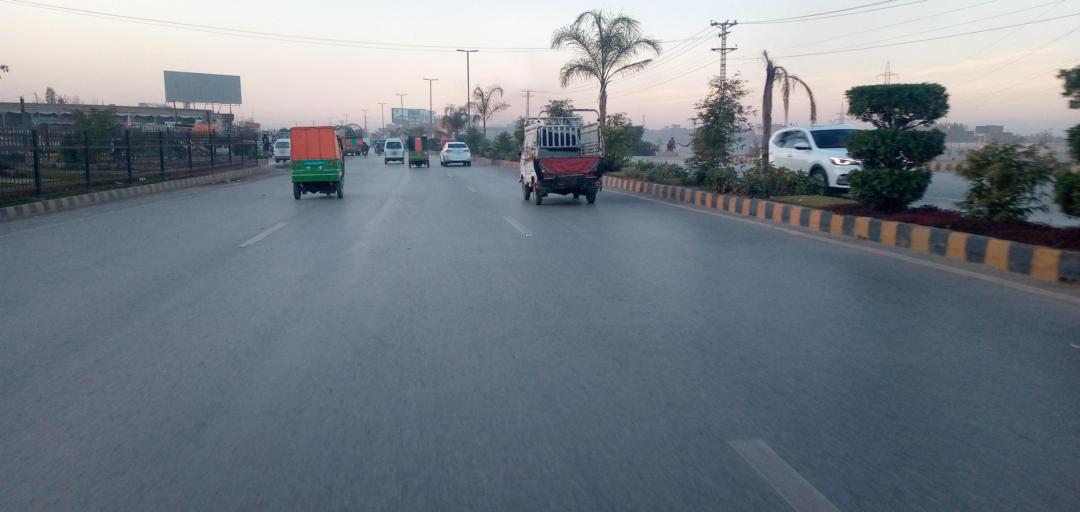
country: PK
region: Khyber Pakhtunkhwa
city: Peshawar
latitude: 34.0268
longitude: 71.6180
